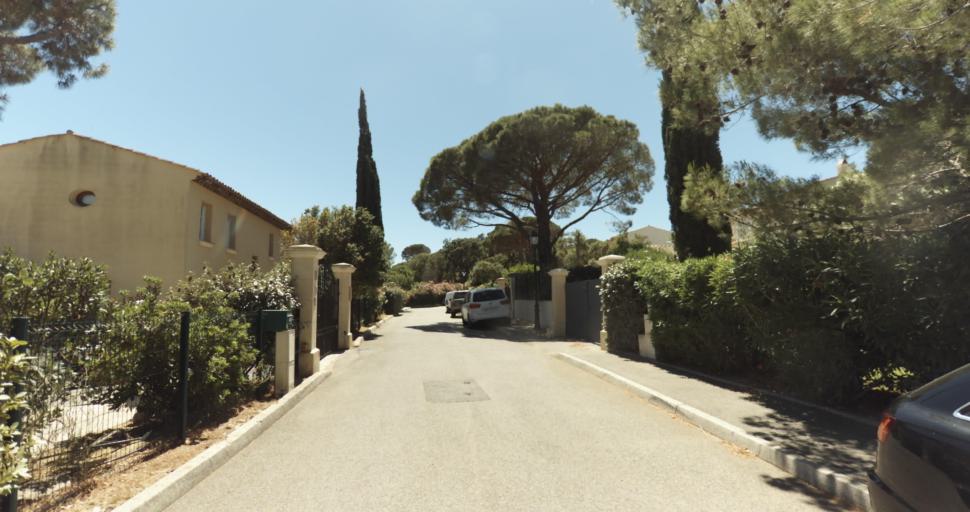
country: FR
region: Provence-Alpes-Cote d'Azur
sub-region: Departement du Var
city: Gassin
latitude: 43.2534
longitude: 6.5706
